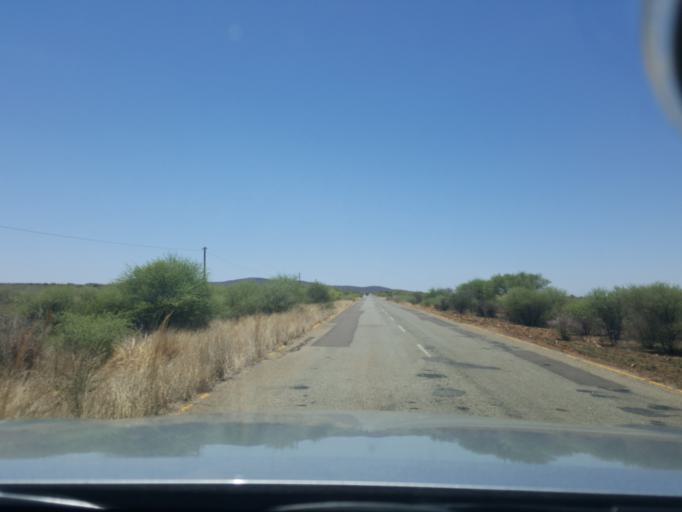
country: BW
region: South East
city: Ramotswa
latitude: -25.0777
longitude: 25.9519
